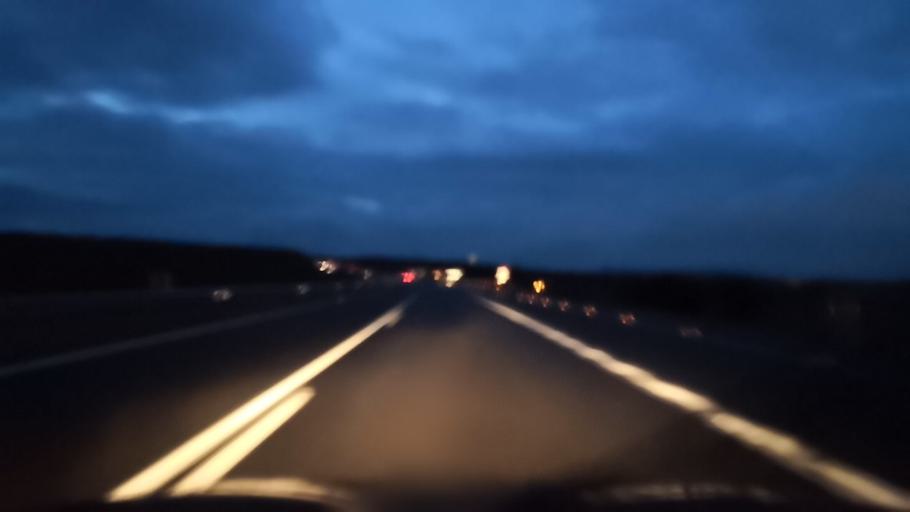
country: ES
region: Extremadura
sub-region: Provincia de Caceres
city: Caceres
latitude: 39.4291
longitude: -6.4040
